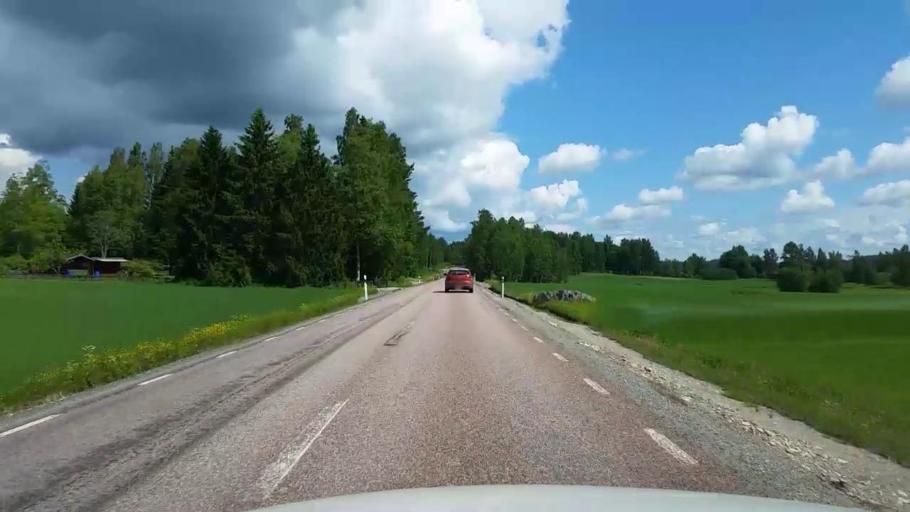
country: SE
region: Vaestmanland
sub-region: Skinnskattebergs Kommun
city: Skinnskatteberg
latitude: 59.7486
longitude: 15.8120
